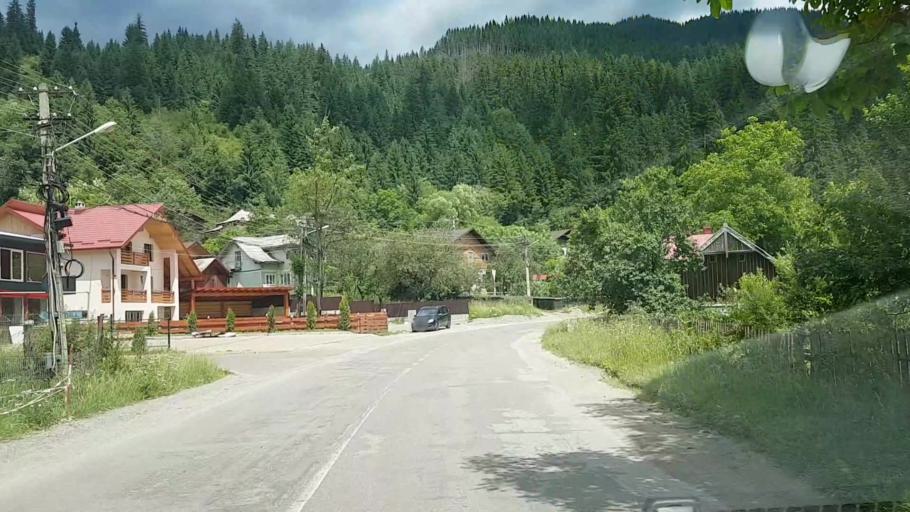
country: RO
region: Suceava
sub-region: Comuna Brosteni
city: Brosteni
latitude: 47.2427
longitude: 25.7023
